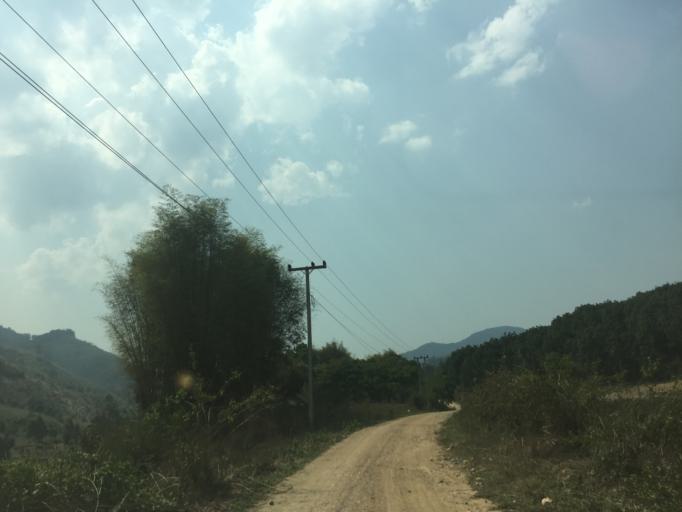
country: TH
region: Nan
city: Song Khwae
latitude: 19.7357
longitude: 100.7238
